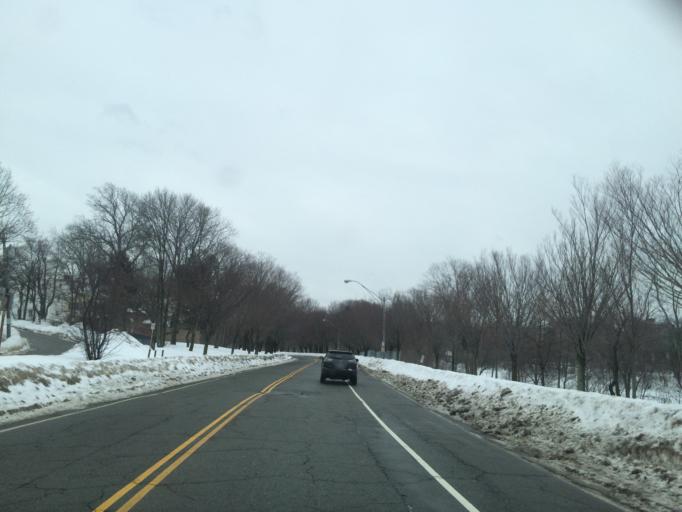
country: US
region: Massachusetts
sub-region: Middlesex County
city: Watertown
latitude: 42.3645
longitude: -71.1839
